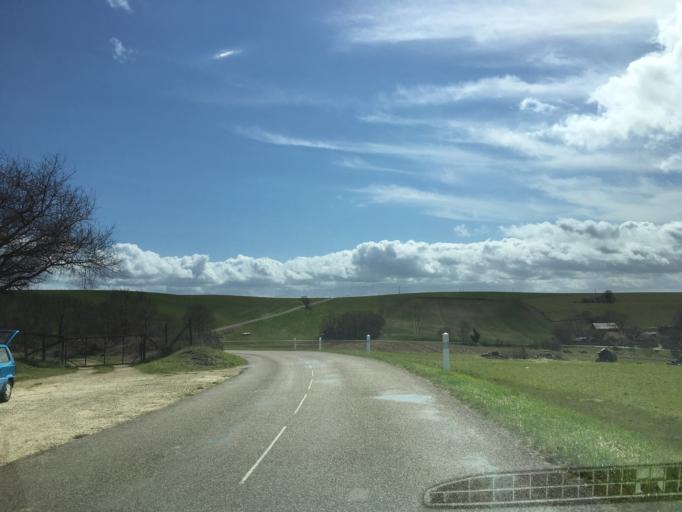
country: FR
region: Bourgogne
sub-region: Departement de l'Yonne
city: Pourrain
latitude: 47.7716
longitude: 3.4101
